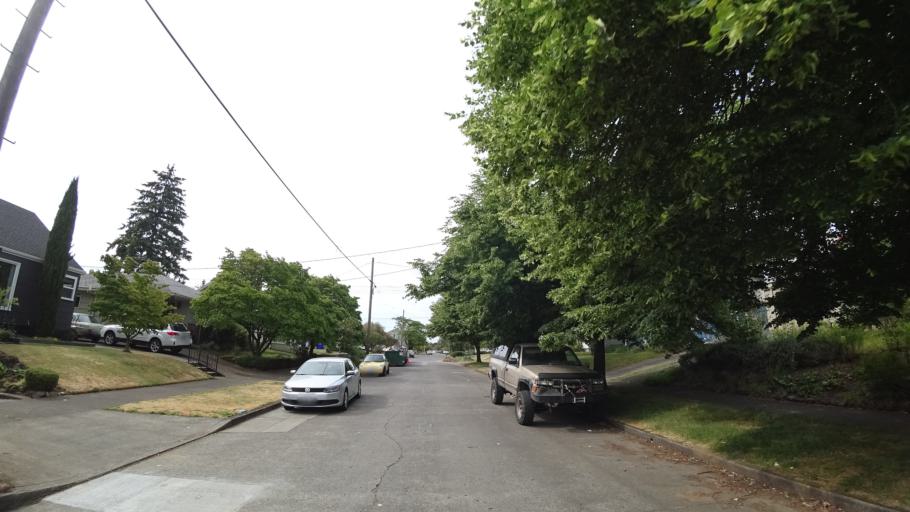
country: US
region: Oregon
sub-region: Multnomah County
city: Portland
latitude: 45.5707
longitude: -122.6863
